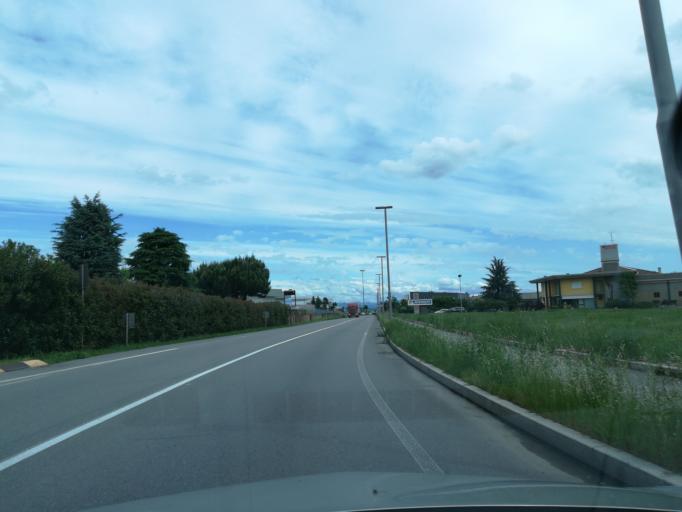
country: IT
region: Lombardy
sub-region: Provincia di Bergamo
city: Antegnate
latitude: 45.4869
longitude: 9.7942
